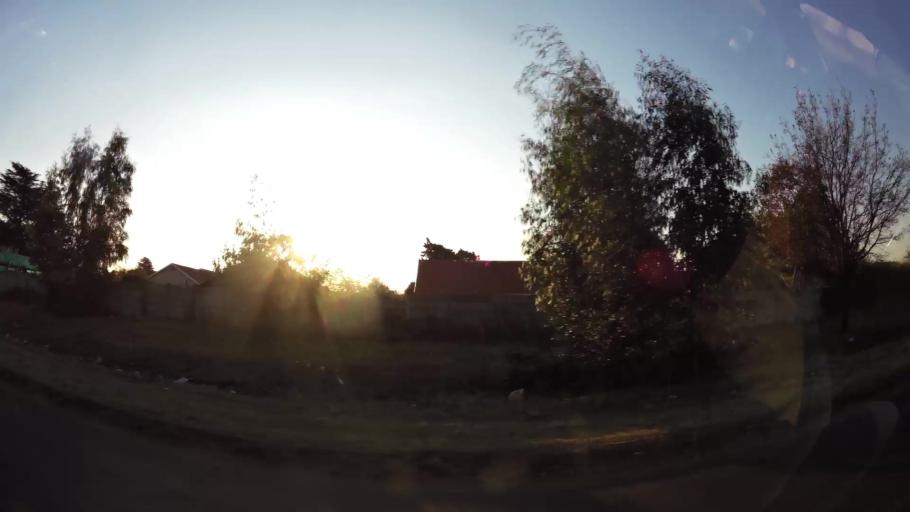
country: ZA
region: Gauteng
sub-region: West Rand District Municipality
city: Randfontein
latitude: -26.2089
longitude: 27.6574
